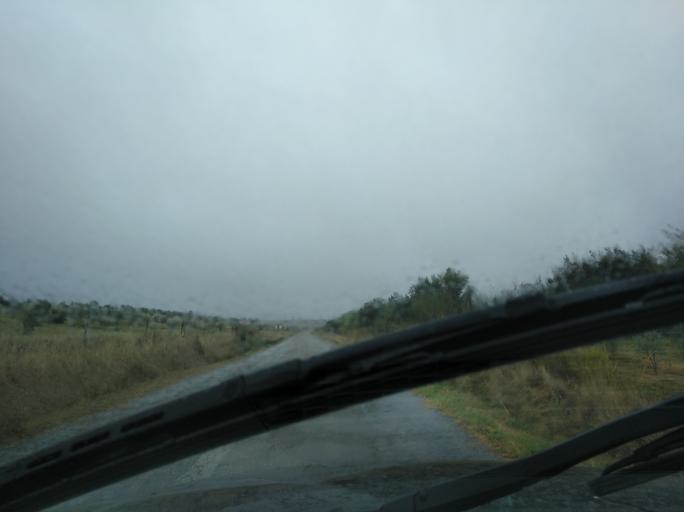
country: PT
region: Portalegre
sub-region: Campo Maior
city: Campo Maior
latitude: 38.9798
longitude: -7.0695
